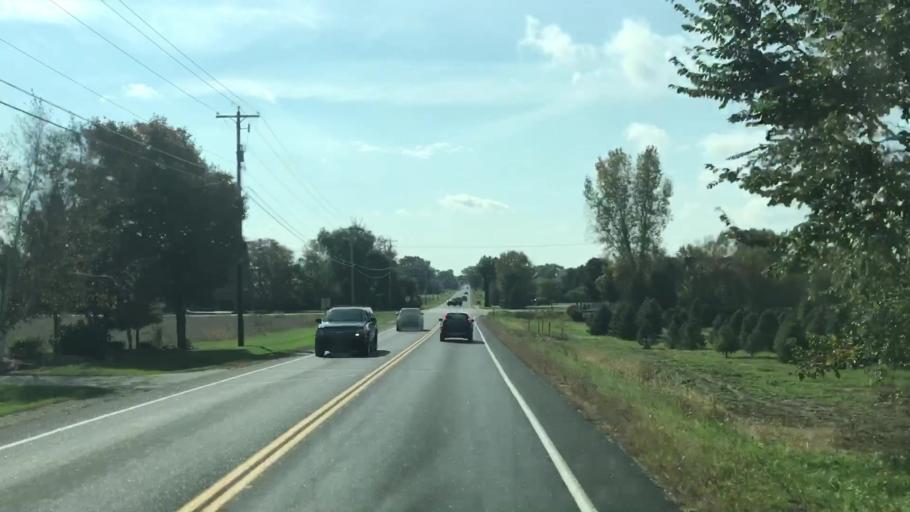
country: US
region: Wisconsin
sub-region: Ozaukee County
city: Mequon
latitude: 43.2081
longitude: -88.0435
